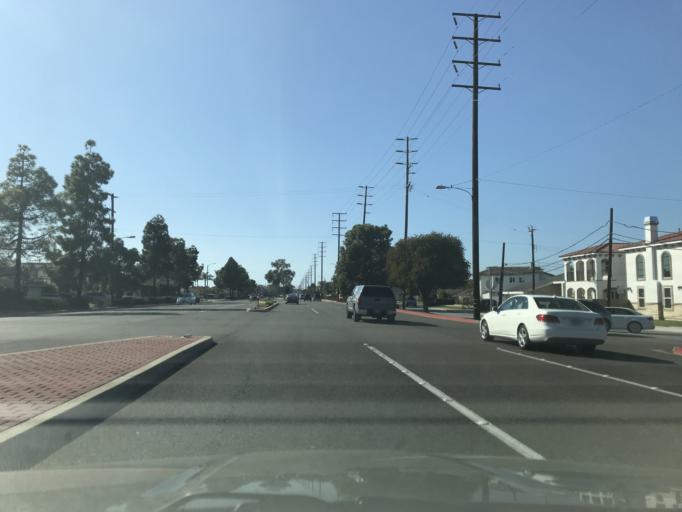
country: US
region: California
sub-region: Orange County
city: Huntington Beach
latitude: 33.6723
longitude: -117.9748
